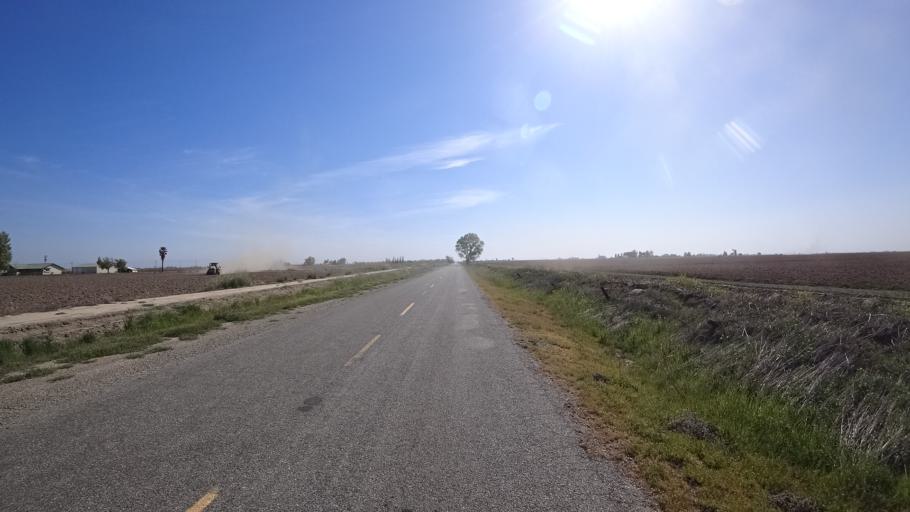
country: US
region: California
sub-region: Glenn County
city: Willows
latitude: 39.5388
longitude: -122.1519
